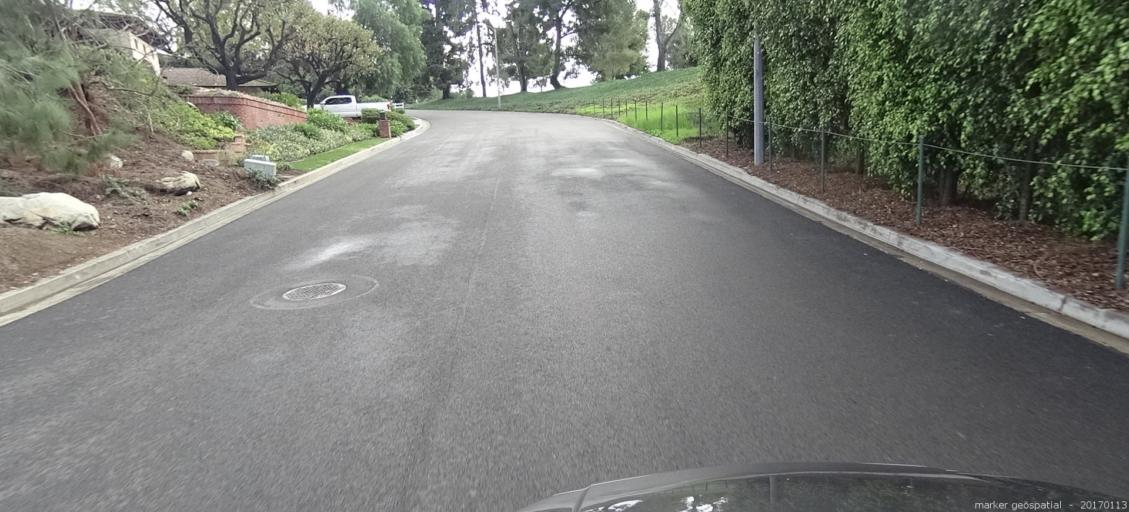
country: US
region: California
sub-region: Orange County
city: Yorba Linda
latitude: 33.8818
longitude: -117.7983
